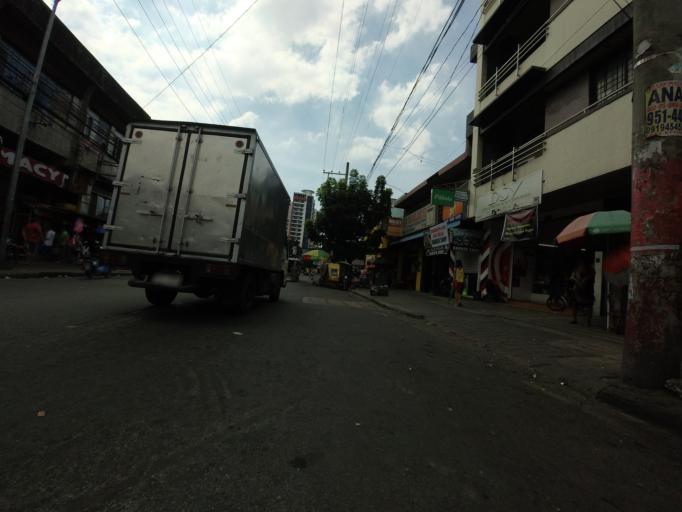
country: PH
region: Metro Manila
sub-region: City of Manila
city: Port Area
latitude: 14.5697
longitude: 120.9885
